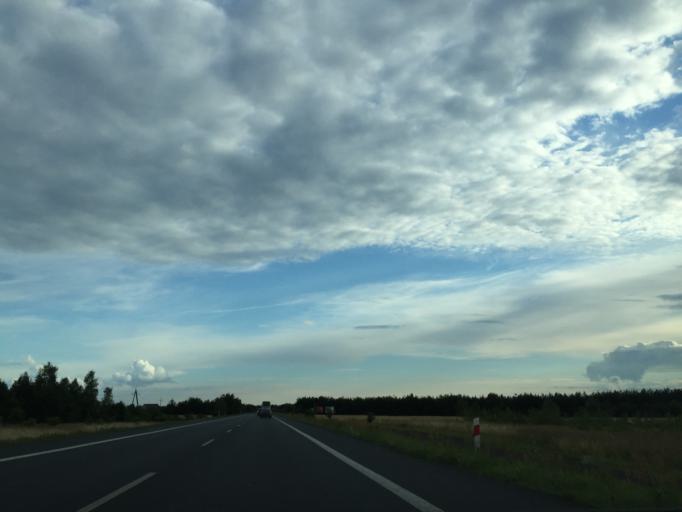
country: PL
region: Lublin Voivodeship
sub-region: Powiat lubartowski
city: Lubartow
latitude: 51.4723
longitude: 22.5844
